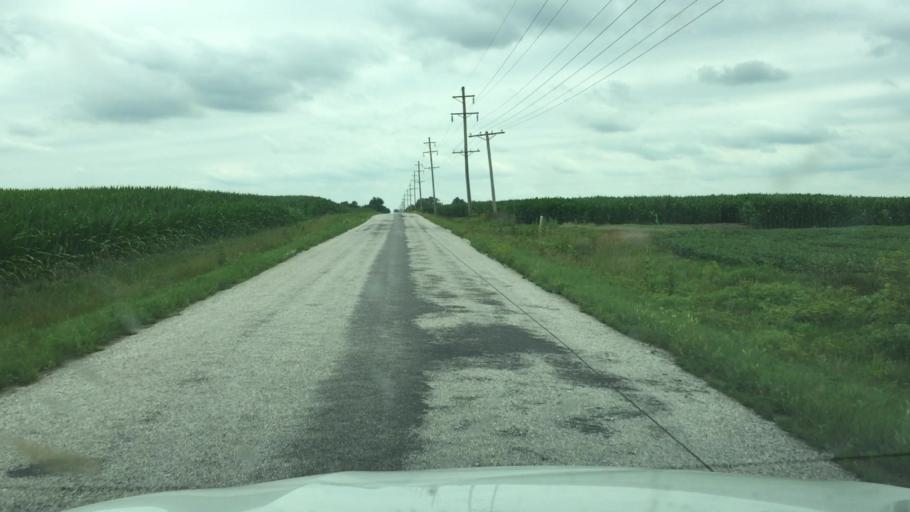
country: US
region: Illinois
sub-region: Hancock County
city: Carthage
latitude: 40.3384
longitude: -91.0824
